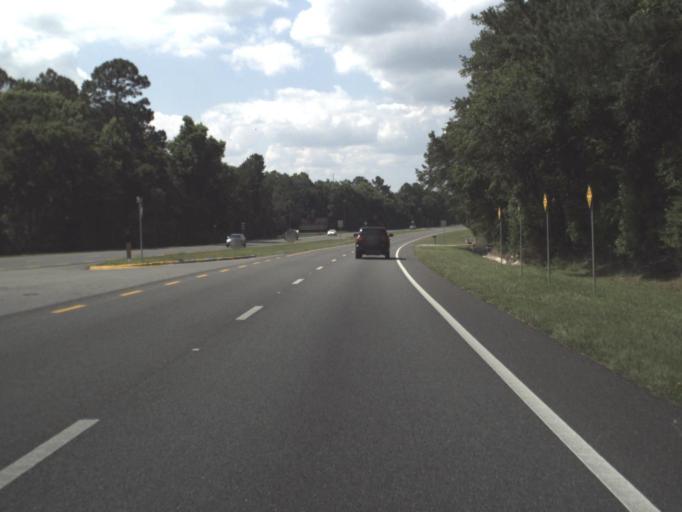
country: US
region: Florida
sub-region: Alachua County
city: Waldo
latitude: 29.7206
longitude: -82.1406
